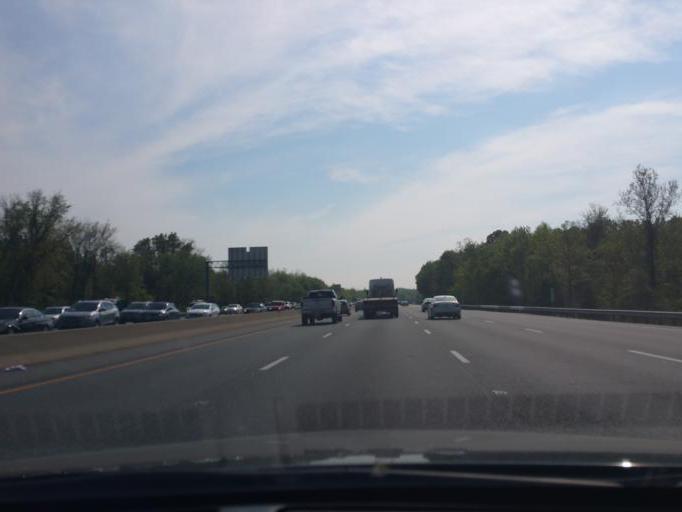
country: US
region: Maryland
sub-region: Harford County
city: Joppatowne
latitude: 39.4523
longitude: -76.3190
